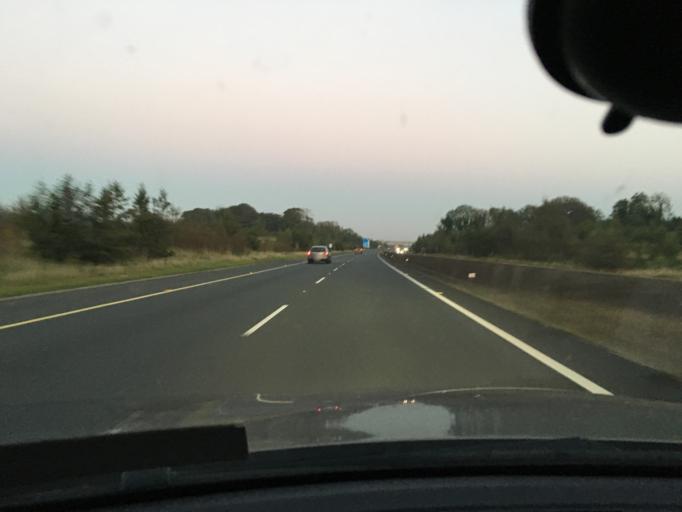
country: IE
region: Connaught
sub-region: County Galway
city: Athenry
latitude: 53.2954
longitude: -8.7856
